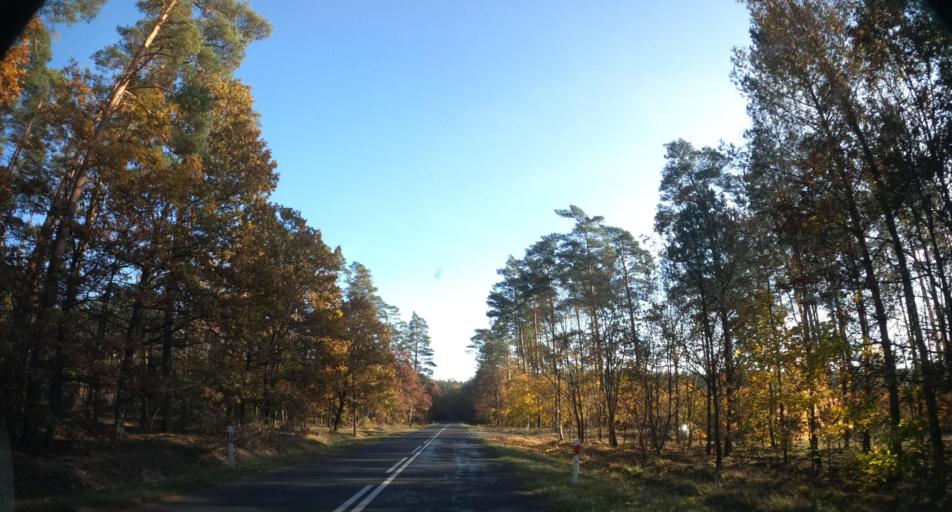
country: PL
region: West Pomeranian Voivodeship
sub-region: Powiat policki
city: Dobra
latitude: 53.5877
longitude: 14.3739
